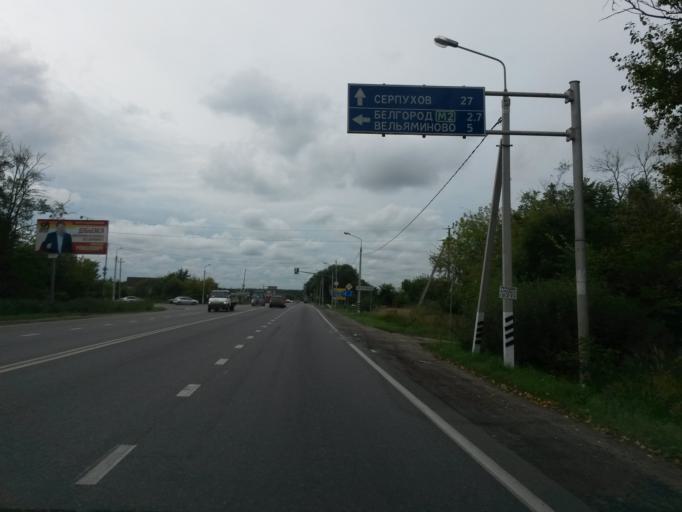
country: RU
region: Moskovskaya
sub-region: Chekhovskiy Rayon
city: Chekhov
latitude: 55.1893
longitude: 37.5010
